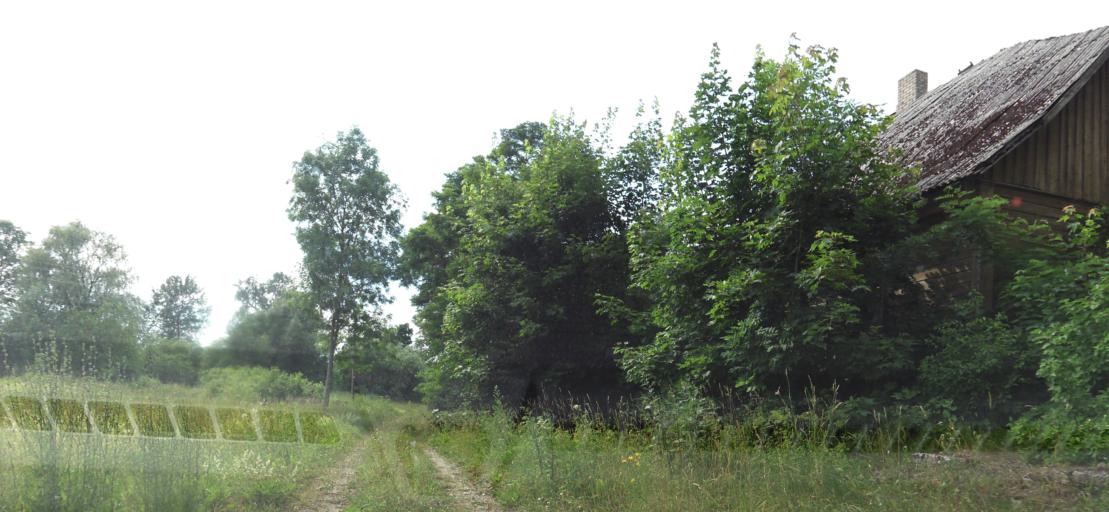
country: LT
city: Obeliai
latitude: 56.1507
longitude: 25.0407
